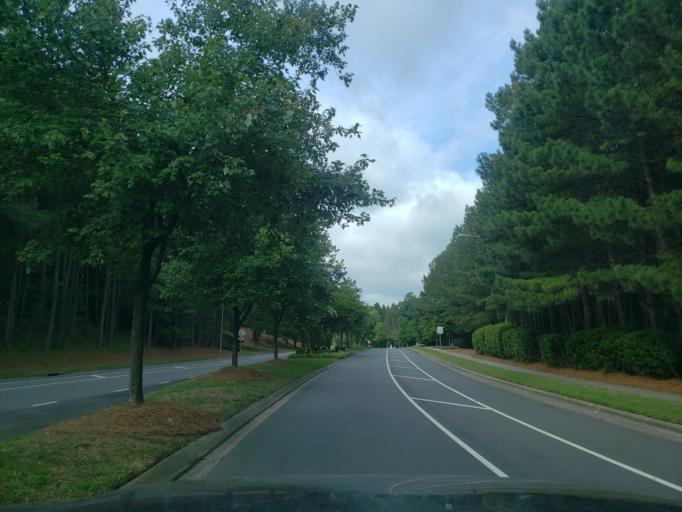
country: US
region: North Carolina
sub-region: Durham County
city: Durham
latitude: 35.9383
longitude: -78.9297
